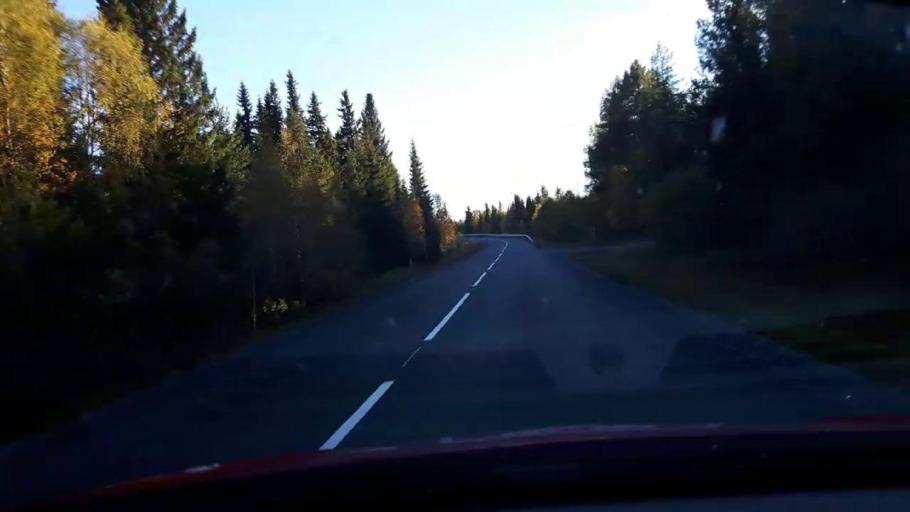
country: SE
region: Jaemtland
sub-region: OEstersunds Kommun
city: Lit
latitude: 63.4580
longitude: 14.8472
